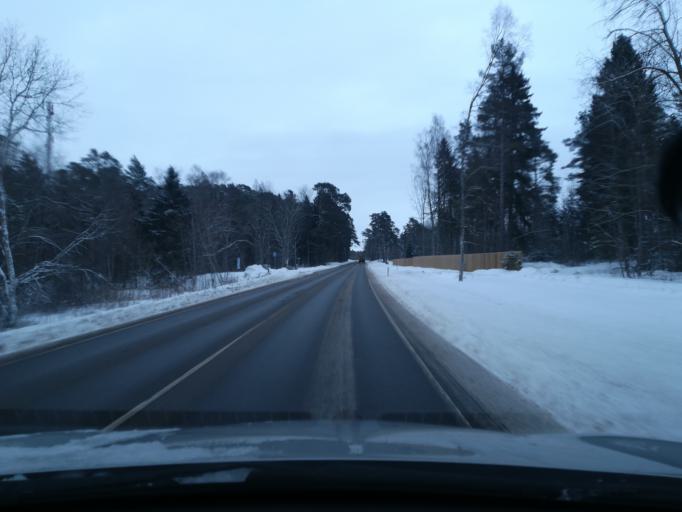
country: EE
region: Harju
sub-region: Keila linn
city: Keila
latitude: 59.3971
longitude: 24.2721
